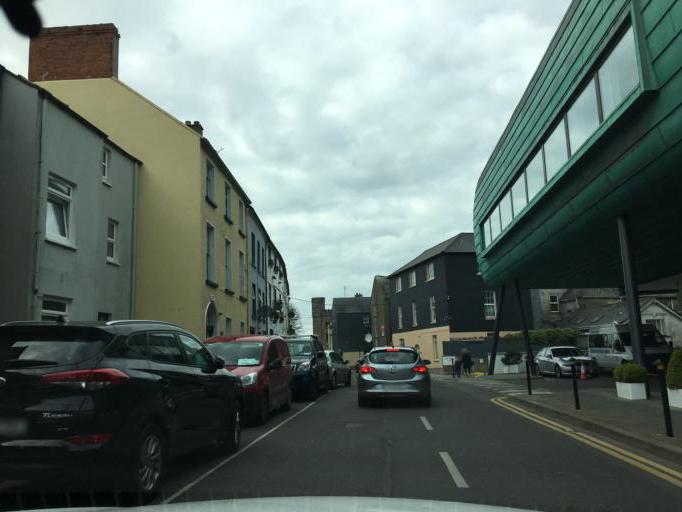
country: IE
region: Leinster
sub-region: Loch Garman
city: Loch Garman
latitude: 52.3402
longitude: -6.4643
